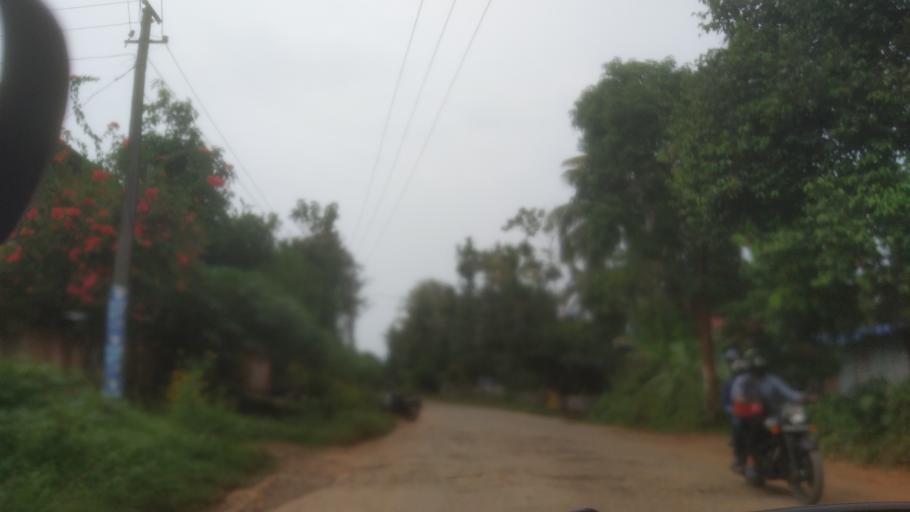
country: IN
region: Kerala
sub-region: Ernakulam
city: Perumbavoor
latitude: 10.0547
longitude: 76.5192
